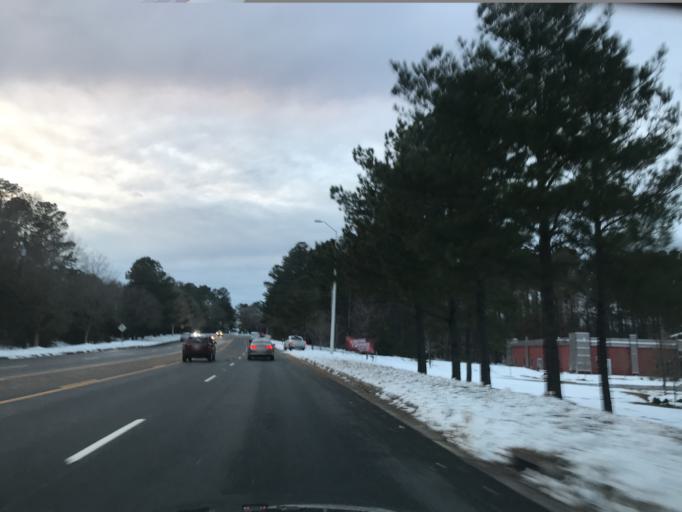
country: US
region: North Carolina
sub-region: Wake County
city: Wake Forest
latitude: 35.8980
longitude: -78.5718
